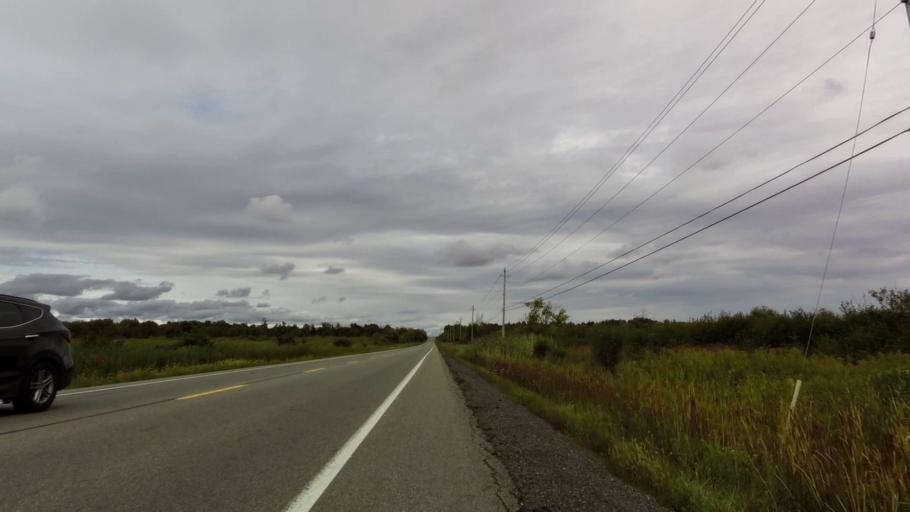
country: CA
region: Ontario
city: Ottawa
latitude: 45.3015
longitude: -75.6672
